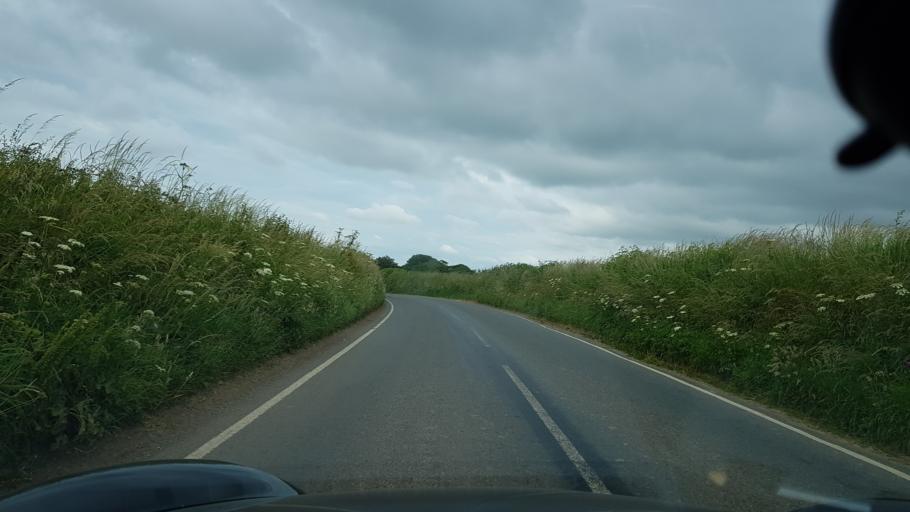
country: GB
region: Wales
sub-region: Pembrokeshire
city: Herbrandston
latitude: 51.7599
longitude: -5.1044
